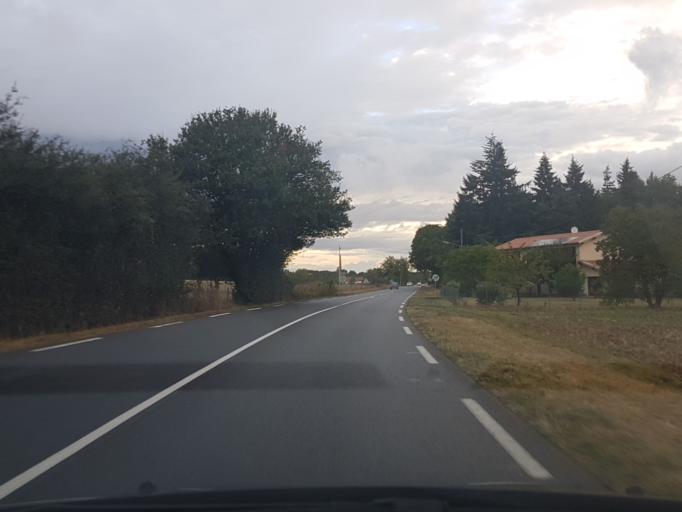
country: FR
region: Midi-Pyrenees
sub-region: Departement de l'Ariege
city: La Tour-du-Crieu
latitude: 43.0866
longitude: 1.7366
